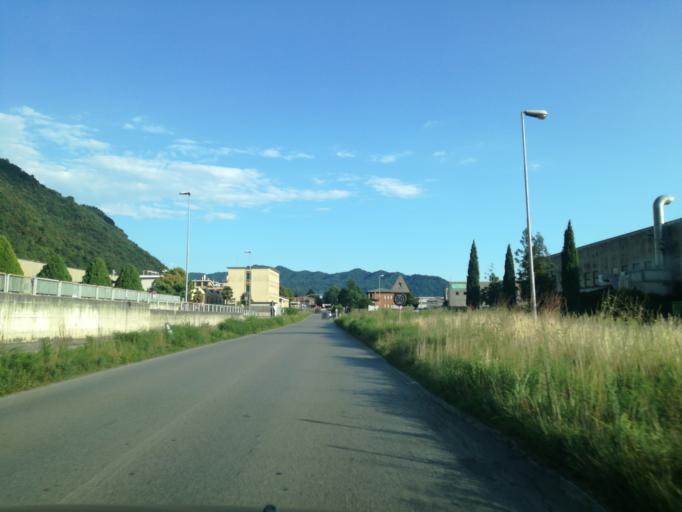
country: IT
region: Lombardy
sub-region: Provincia di Lecco
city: Monte Marenzo
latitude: 45.7653
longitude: 9.4461
